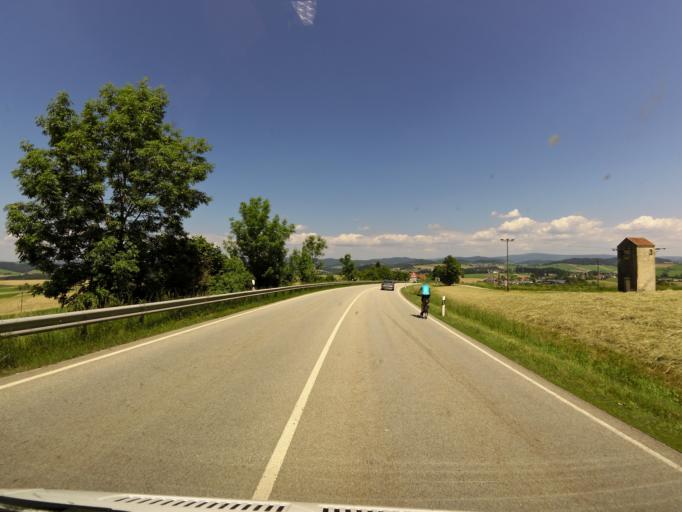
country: DE
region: Bavaria
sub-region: Lower Bavaria
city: Roehrnbach
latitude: 48.7093
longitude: 13.5222
